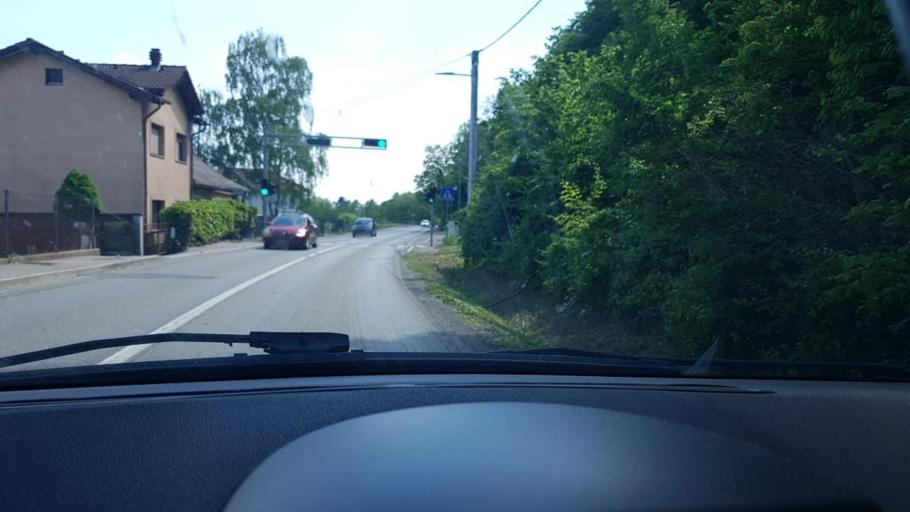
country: HR
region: Grad Zagreb
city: Dubrava
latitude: 45.8446
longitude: 16.0287
